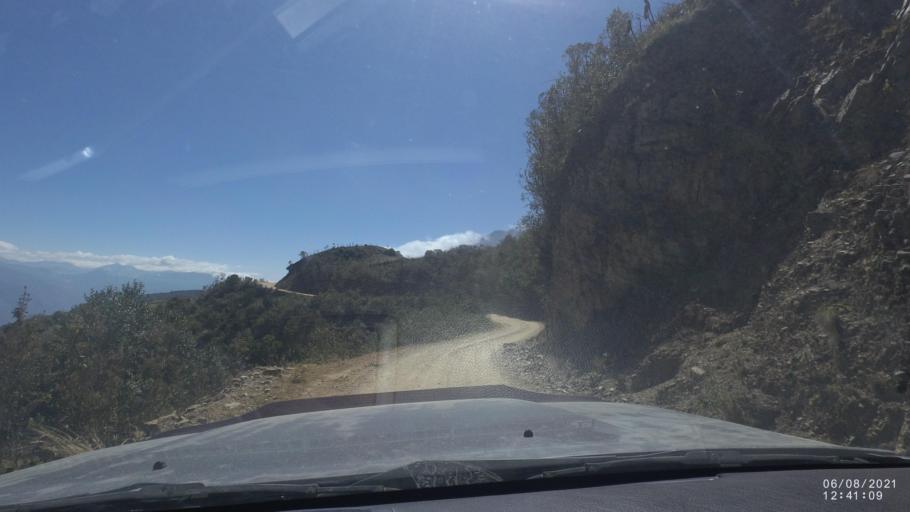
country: BO
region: Cochabamba
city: Colchani
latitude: -16.7831
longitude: -66.6663
